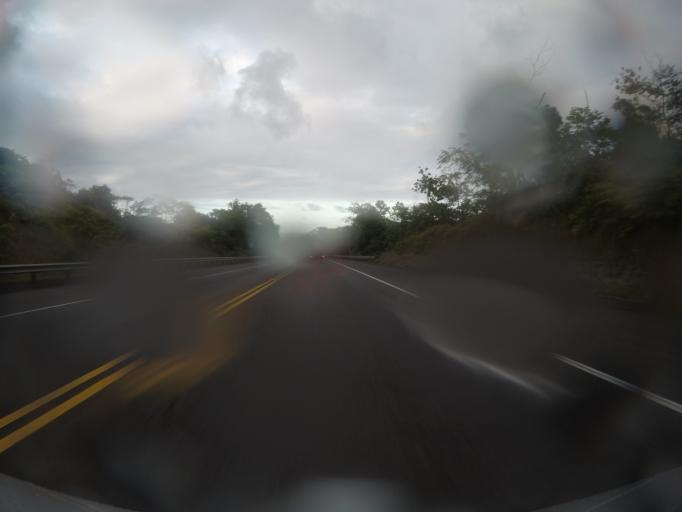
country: US
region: Hawaii
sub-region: Hawaii County
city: Hilo
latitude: 19.6802
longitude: -155.1251
